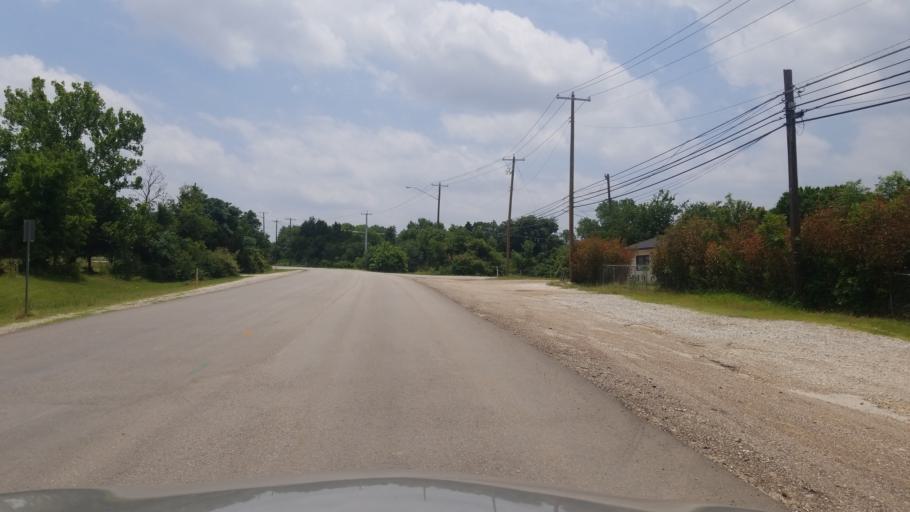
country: US
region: Texas
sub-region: Dallas County
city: Duncanville
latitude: 32.6929
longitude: -96.9230
